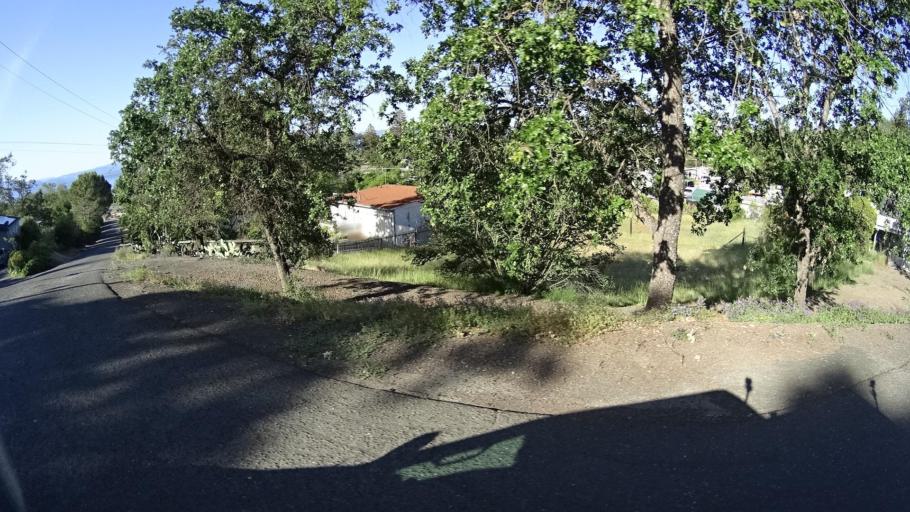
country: US
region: California
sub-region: Lake County
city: Nice
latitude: 39.1248
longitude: -122.8435
